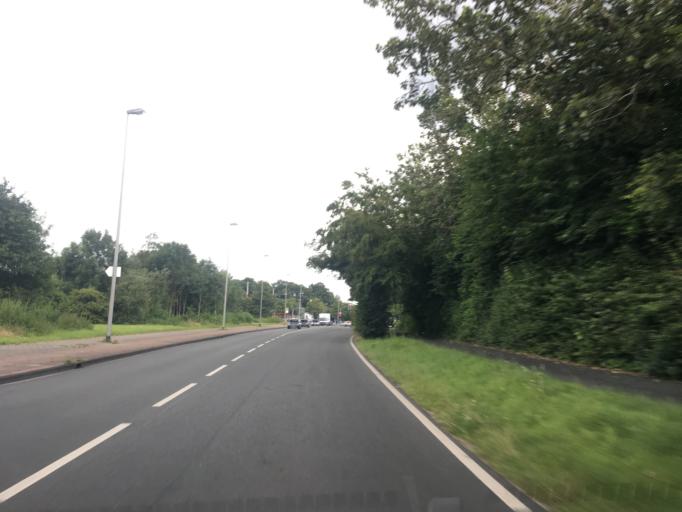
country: DE
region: North Rhine-Westphalia
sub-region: Regierungsbezirk Munster
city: Muenster
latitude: 51.9302
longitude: 7.6466
